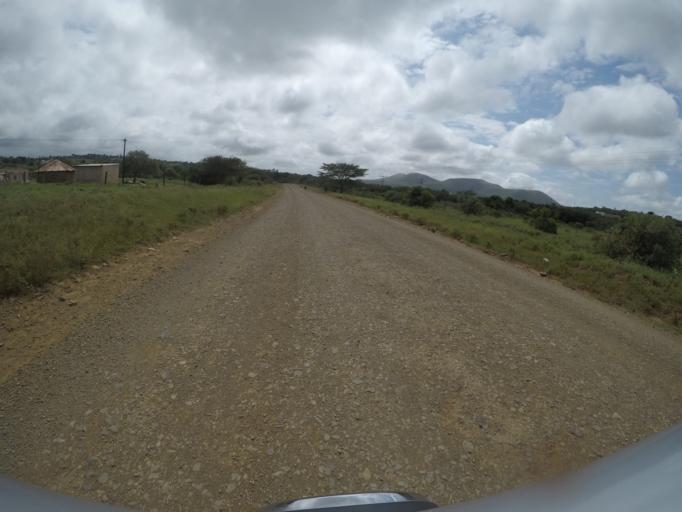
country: ZA
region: KwaZulu-Natal
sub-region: uThungulu District Municipality
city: Empangeni
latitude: -28.5909
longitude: 31.8408
